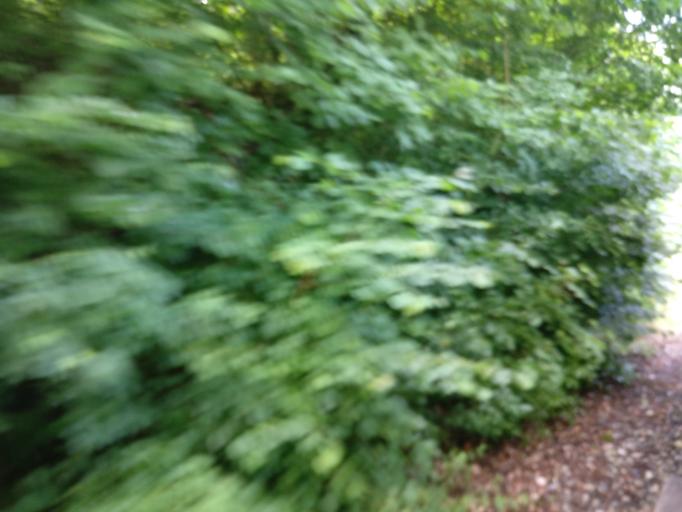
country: AT
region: Upper Austria
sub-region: Politischer Bezirk Steyr-Land
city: Waldneukirchen
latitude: 48.0028
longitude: 14.2959
